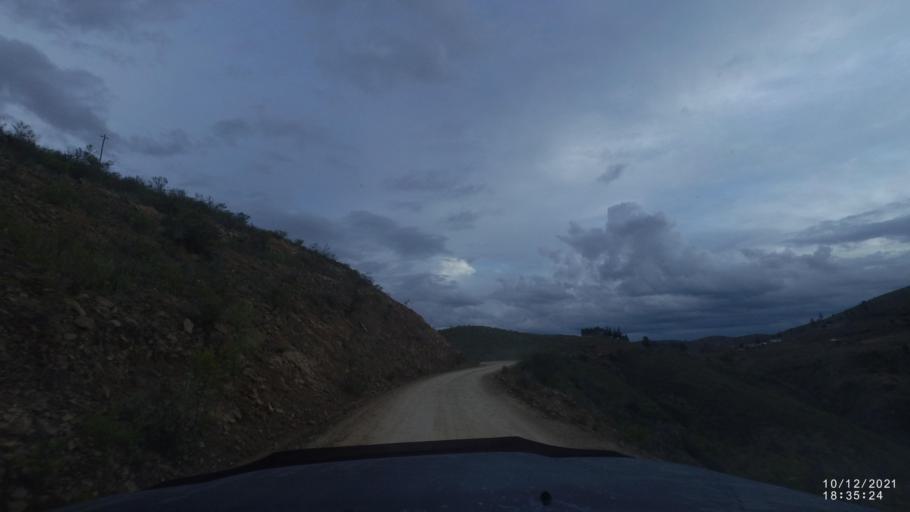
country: BO
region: Cochabamba
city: Tarata
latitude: -17.8276
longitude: -65.9909
